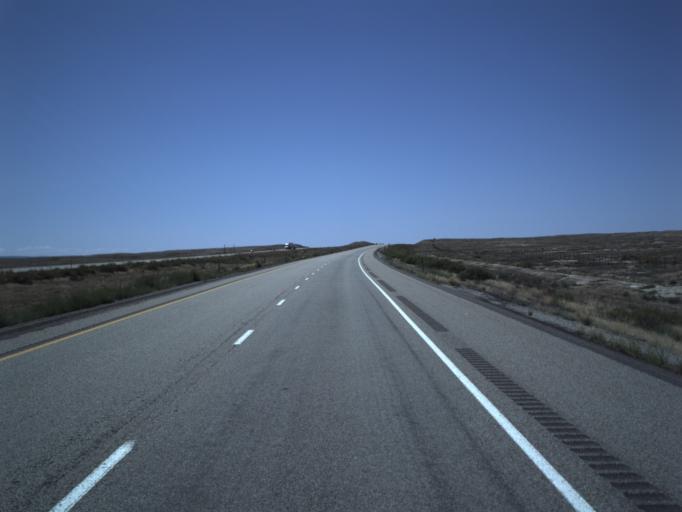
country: US
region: Utah
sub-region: Grand County
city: Moab
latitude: 39.0127
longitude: -109.3063
